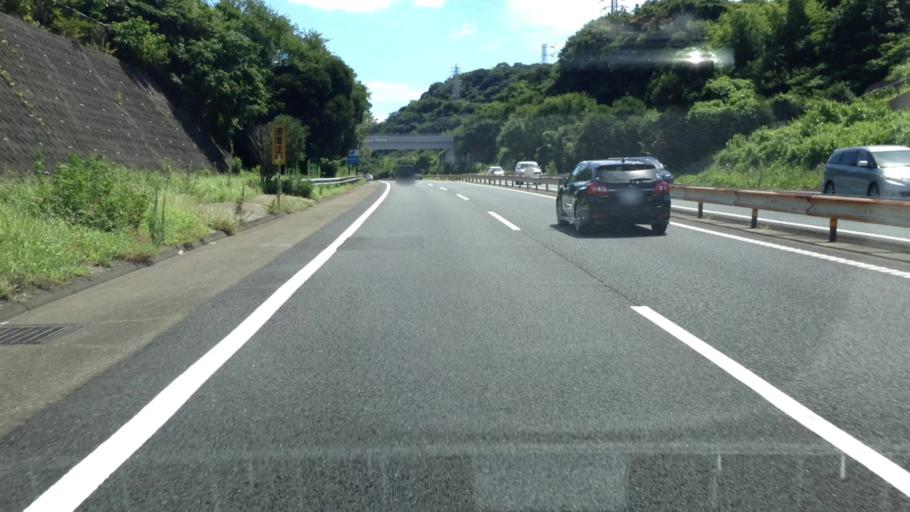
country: JP
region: Kanagawa
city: Yokosuka
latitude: 35.2609
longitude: 139.6333
